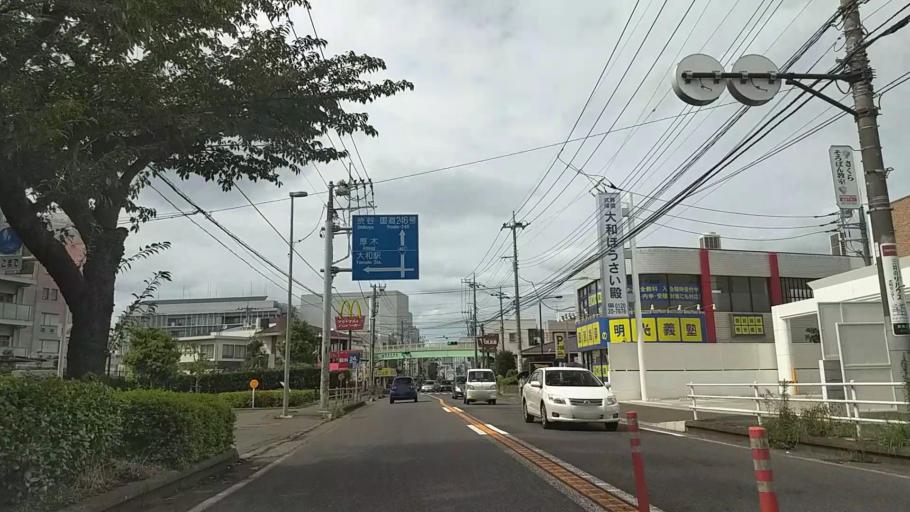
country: JP
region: Kanagawa
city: Minami-rinkan
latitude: 35.4672
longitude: 139.4663
